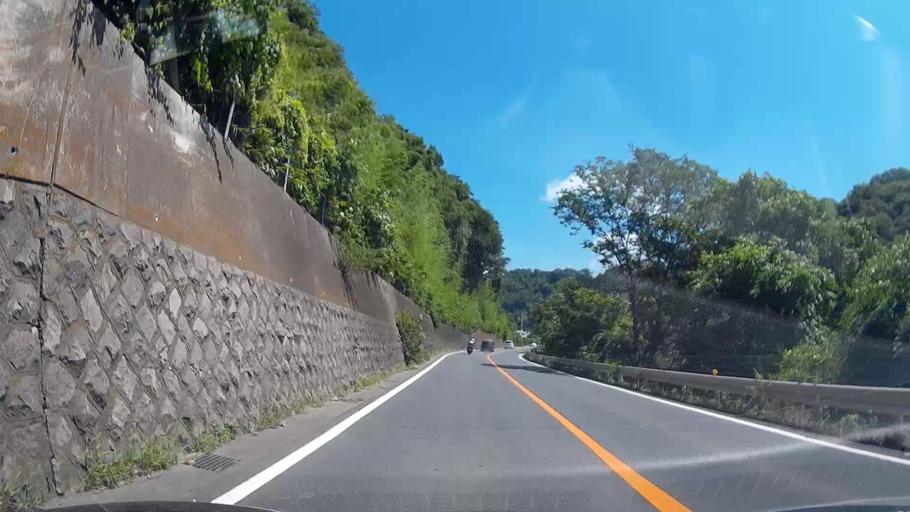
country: JP
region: Gunma
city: Numata
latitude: 36.6263
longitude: 139.0356
